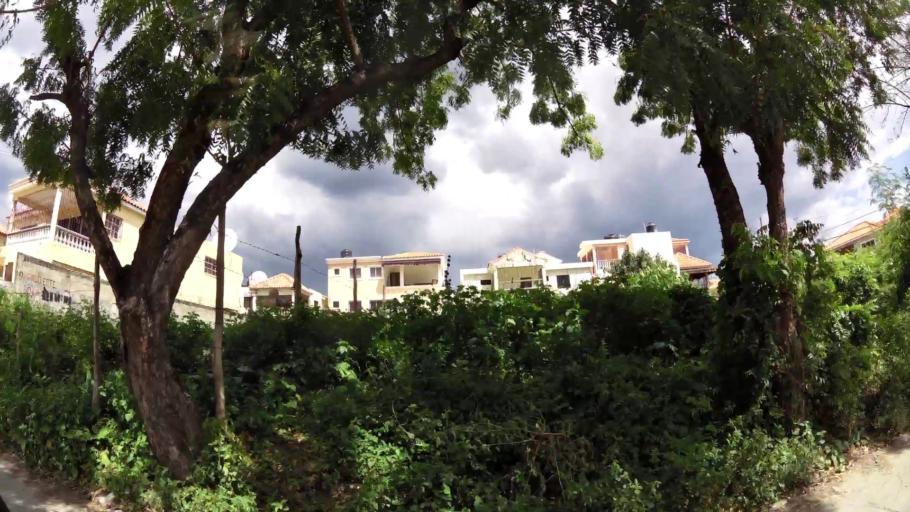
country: DO
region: San Cristobal
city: San Cristobal
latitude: 18.4169
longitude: -70.1038
